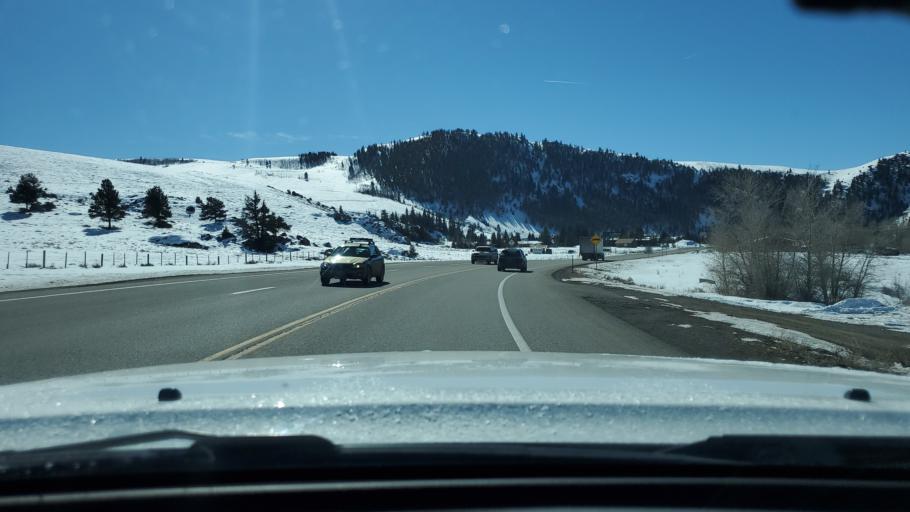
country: US
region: Colorado
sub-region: Gunnison County
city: Gunnison
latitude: 38.6704
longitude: -106.8457
